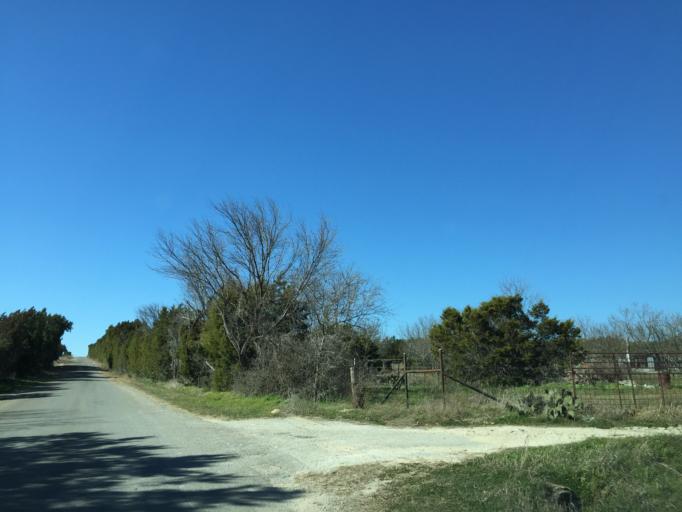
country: US
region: Texas
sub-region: Burnet County
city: Bertram
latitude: 30.9028
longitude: -98.1057
